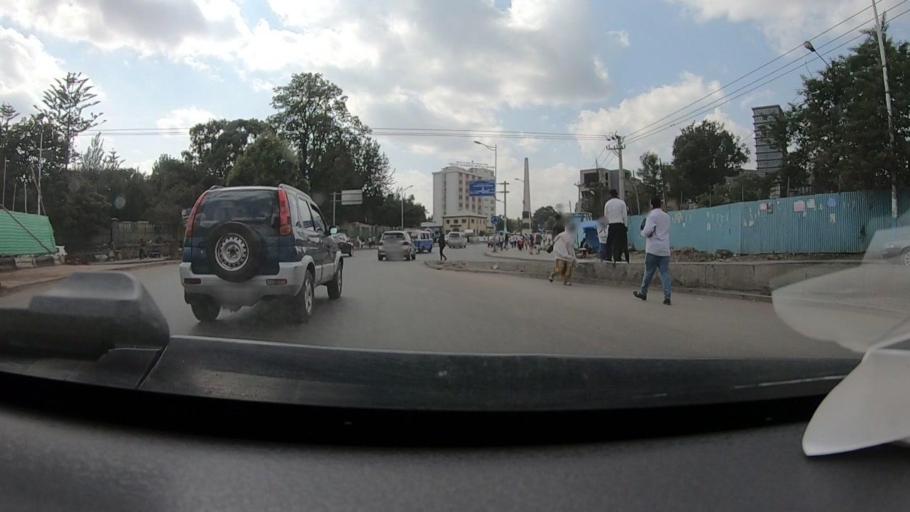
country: ET
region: Adis Abeba
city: Addis Ababa
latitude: 9.0437
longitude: 38.7626
